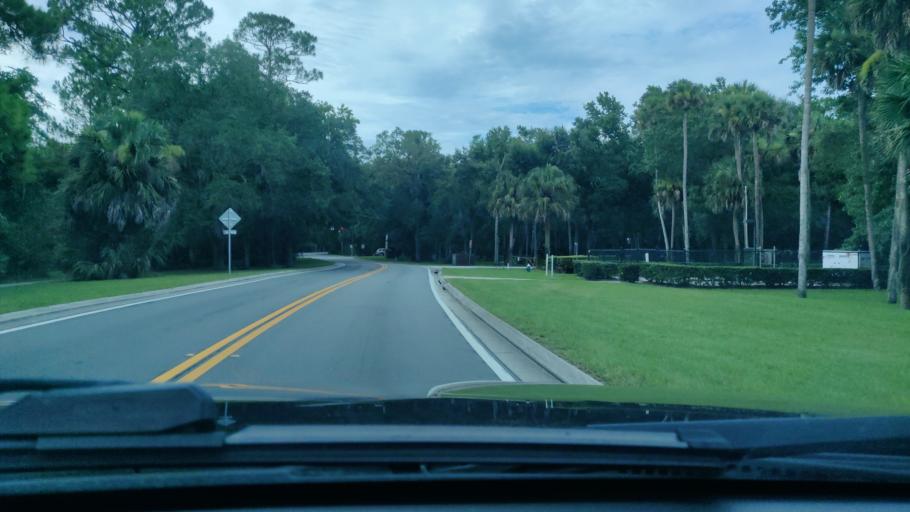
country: US
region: Florida
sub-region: Flagler County
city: Palm Coast
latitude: 29.5555
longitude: -81.1972
